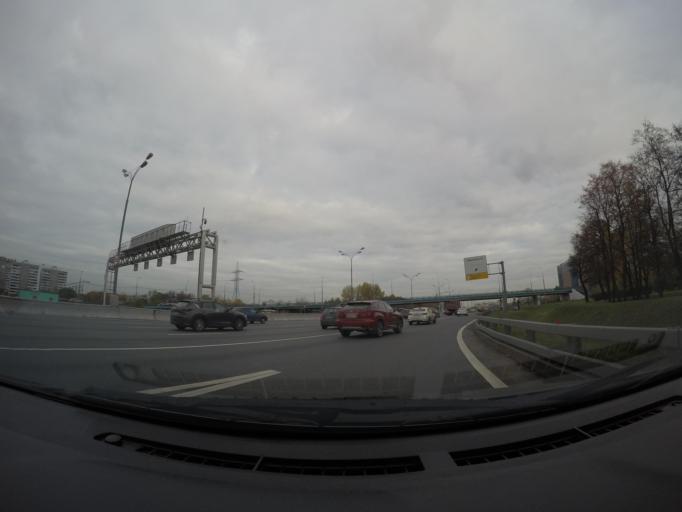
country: RU
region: Moscow
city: Ivanovskoye
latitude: 55.7677
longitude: 37.8434
